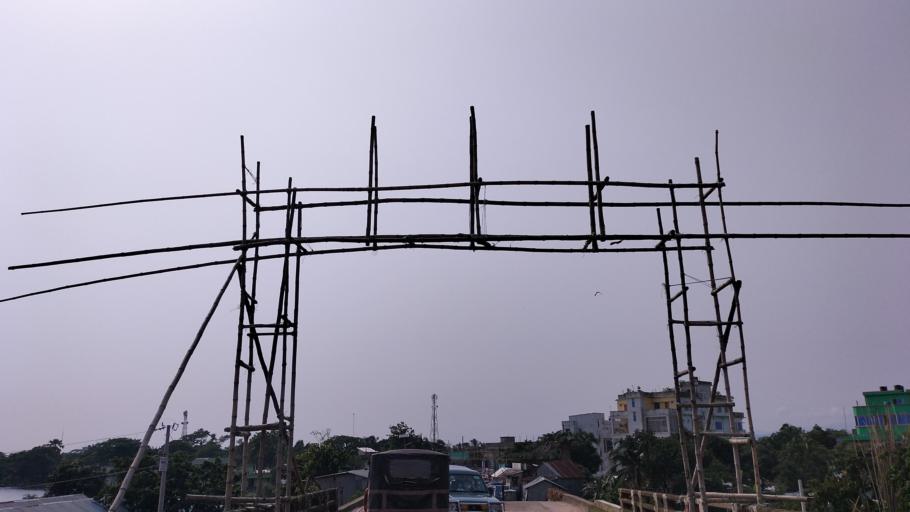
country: BD
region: Dhaka
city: Netrakona
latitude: 25.0756
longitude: 90.8899
